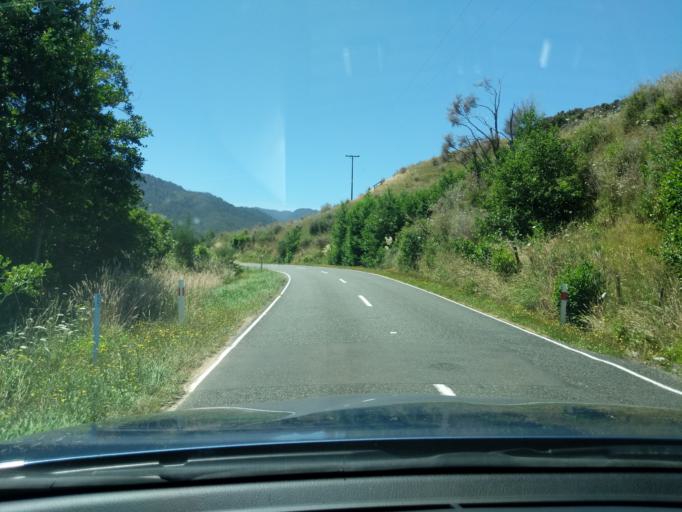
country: NZ
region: Tasman
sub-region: Tasman District
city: Takaka
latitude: -40.7354
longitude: 172.5818
